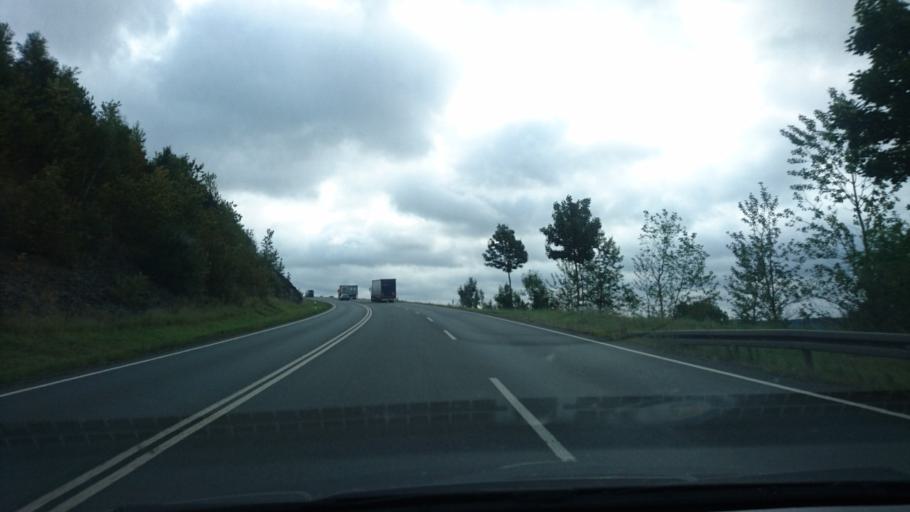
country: DE
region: Bavaria
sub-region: Upper Franconia
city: Selbitz
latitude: 50.3194
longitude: 11.7295
